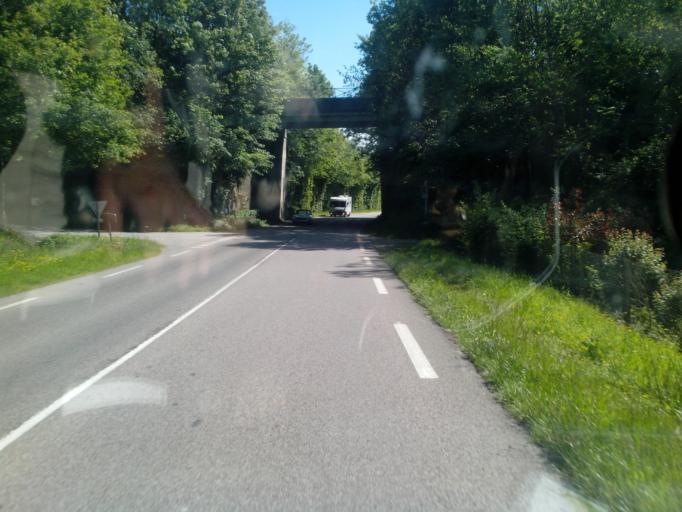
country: FR
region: Lower Normandy
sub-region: Departement du Calvados
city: Saint-Gatien-des-Bois
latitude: 49.3083
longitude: 0.2589
